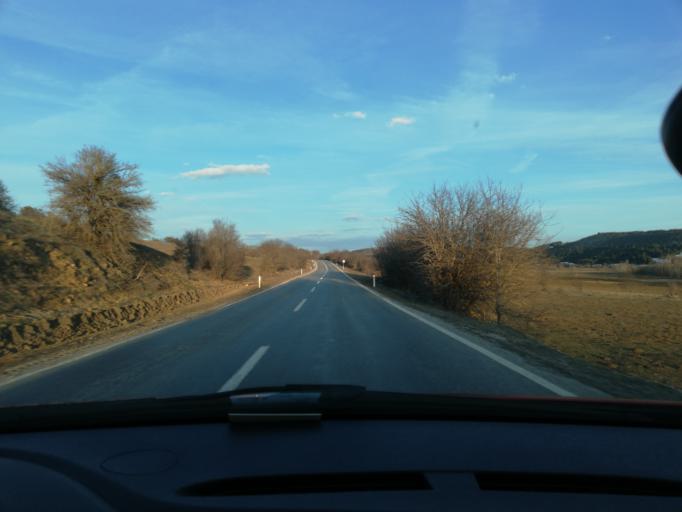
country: TR
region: Kastamonu
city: Agli
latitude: 41.6921
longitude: 33.5971
